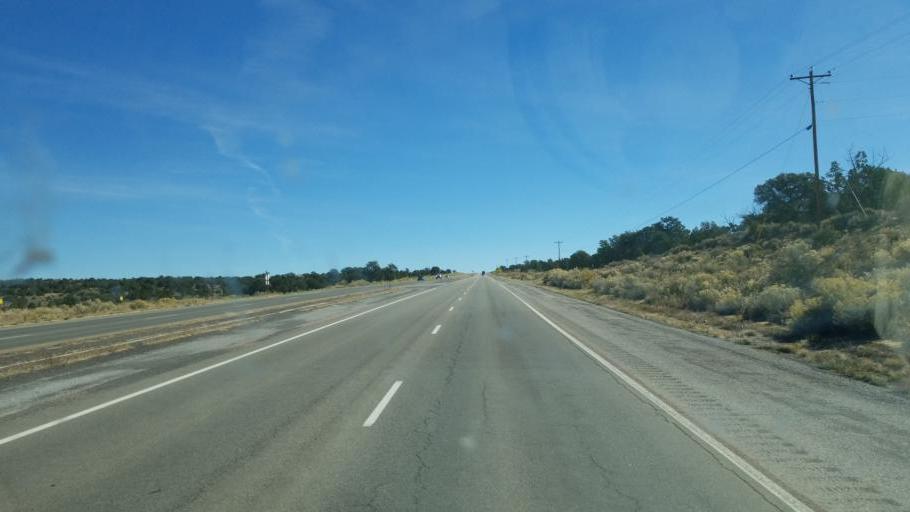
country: US
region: New Mexico
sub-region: McKinley County
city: Twin Lakes
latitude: 35.6354
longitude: -108.8804
